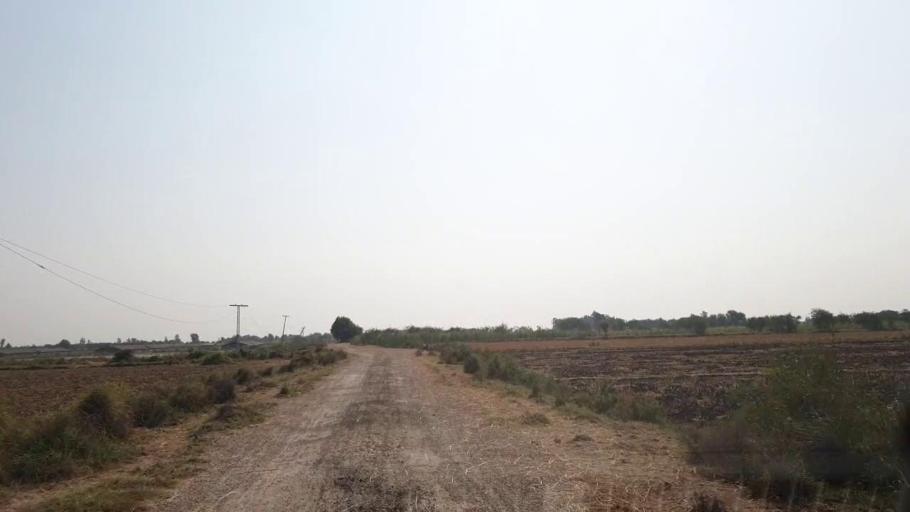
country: PK
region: Sindh
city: Tando Muhammad Khan
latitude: 25.0445
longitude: 68.4525
